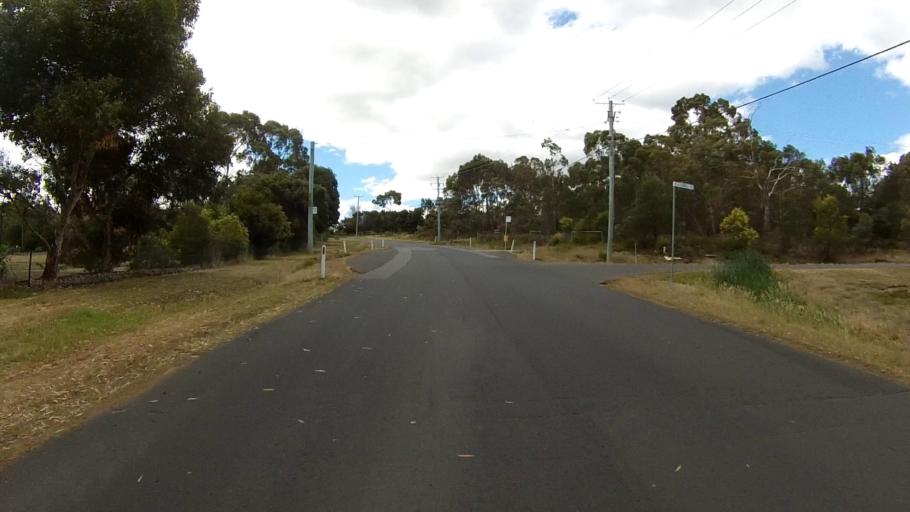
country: AU
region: Tasmania
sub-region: Clarence
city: Acton Park
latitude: -42.8777
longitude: 147.4905
